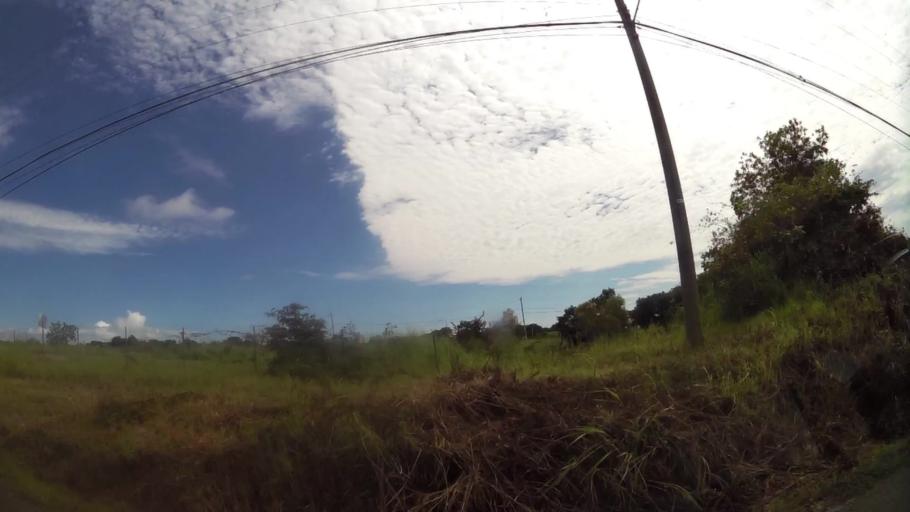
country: PA
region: Panama
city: Nueva Gorgona
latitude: 8.5392
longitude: -79.8988
